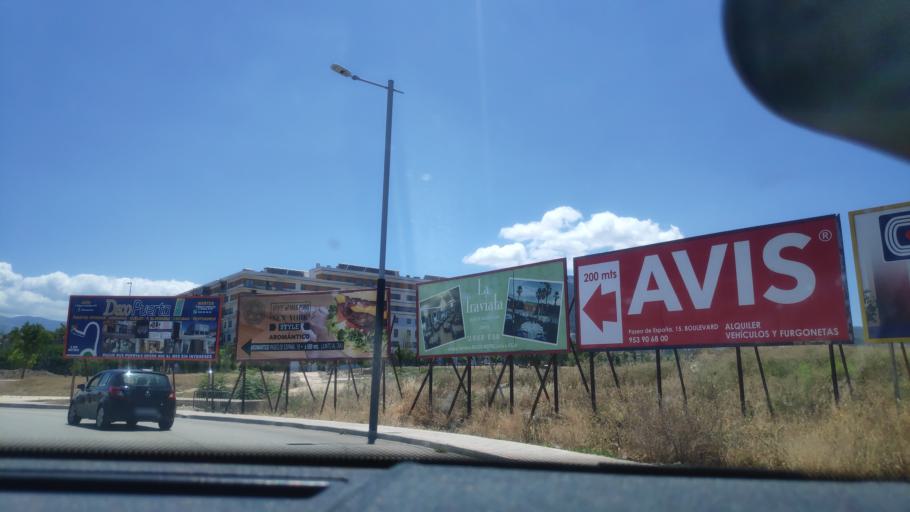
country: ES
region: Andalusia
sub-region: Provincia de Jaen
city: Jaen
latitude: 37.7916
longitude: -3.7918
